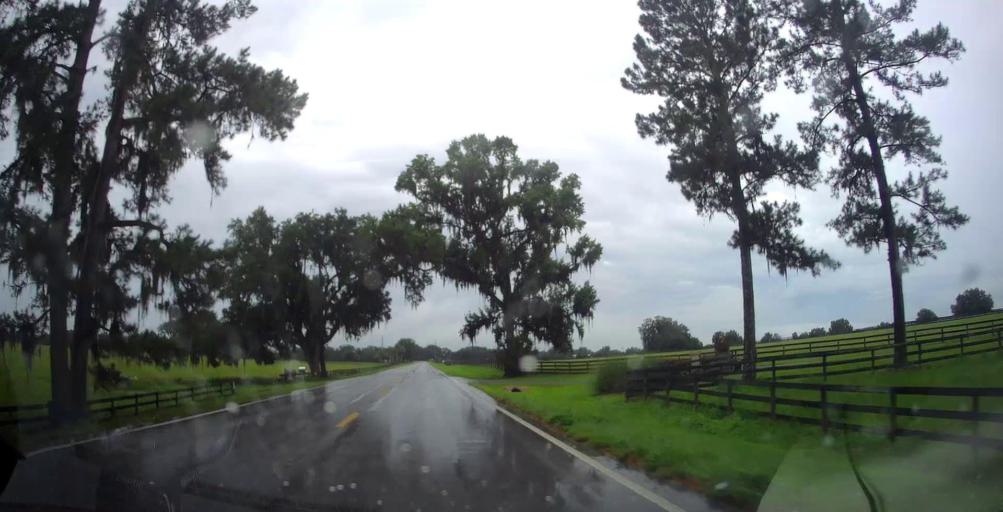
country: US
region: Florida
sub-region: Marion County
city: Citra
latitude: 29.3359
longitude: -82.2091
